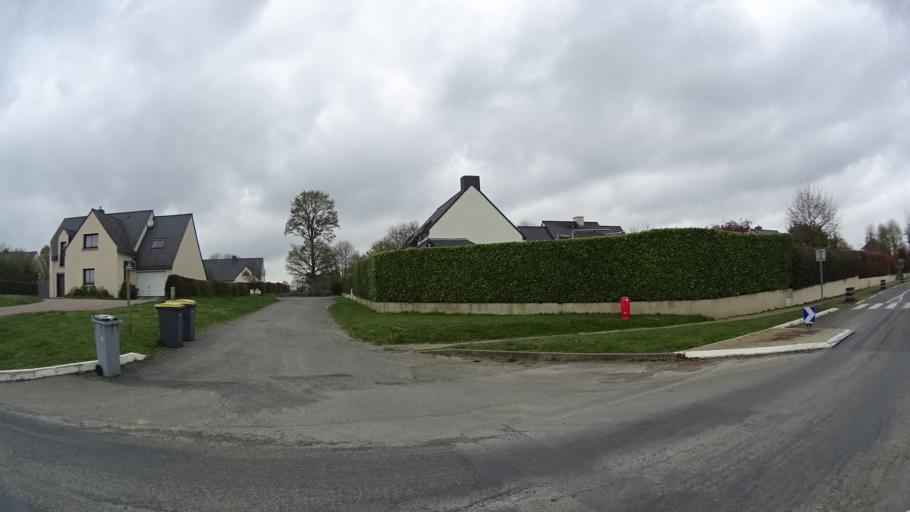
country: FR
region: Brittany
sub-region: Departement d'Ille-et-Vilaine
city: Cintre
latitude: 48.1036
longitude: -1.8768
